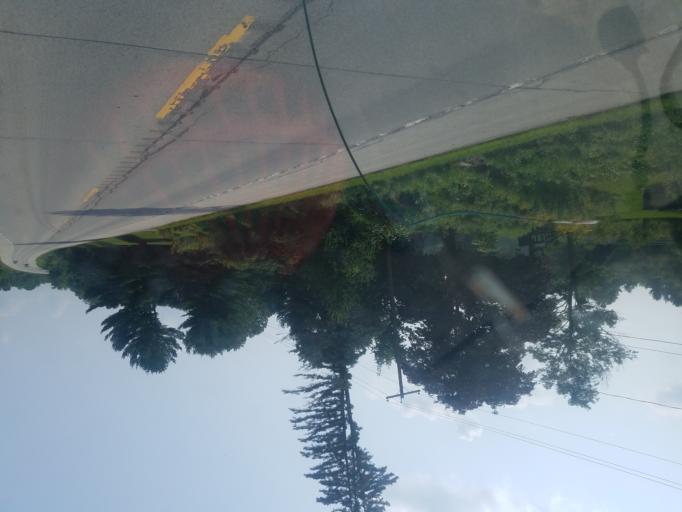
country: US
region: New York
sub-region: Montgomery County
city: Tribes Hill
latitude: 42.9328
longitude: -74.3244
